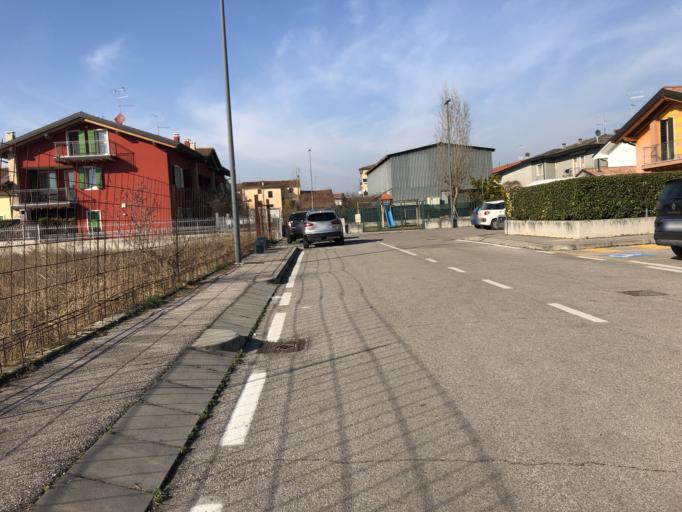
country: IT
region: Veneto
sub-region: Provincia di Verona
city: Lugagnano
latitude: 45.4305
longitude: 10.8781
